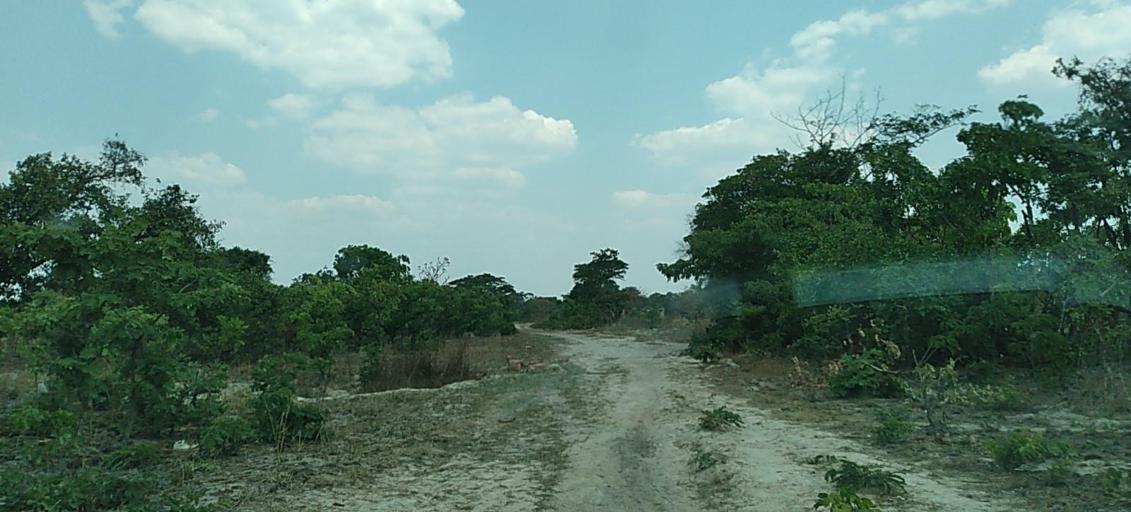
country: CD
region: Katanga
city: Kipushi
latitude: -11.9915
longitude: 27.4173
